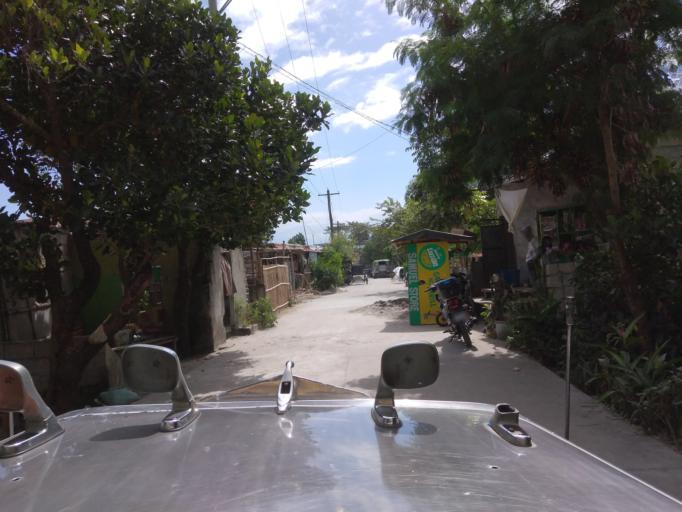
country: PH
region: Central Luzon
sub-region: Province of Pampanga
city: Anao
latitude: 15.1185
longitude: 120.7018
